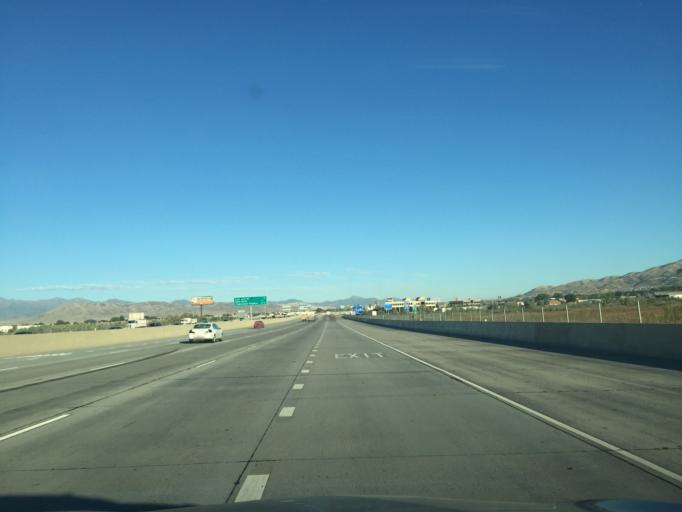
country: US
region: Utah
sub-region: Utah County
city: Lehi
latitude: 40.3807
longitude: -111.8249
